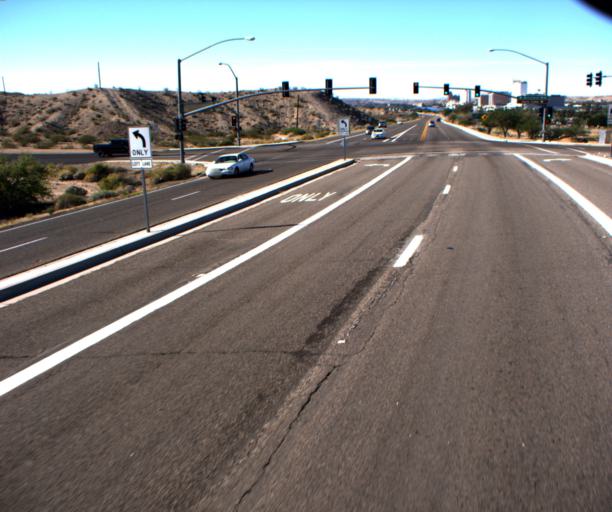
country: US
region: Nevada
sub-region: Clark County
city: Laughlin
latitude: 35.1836
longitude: -114.5633
